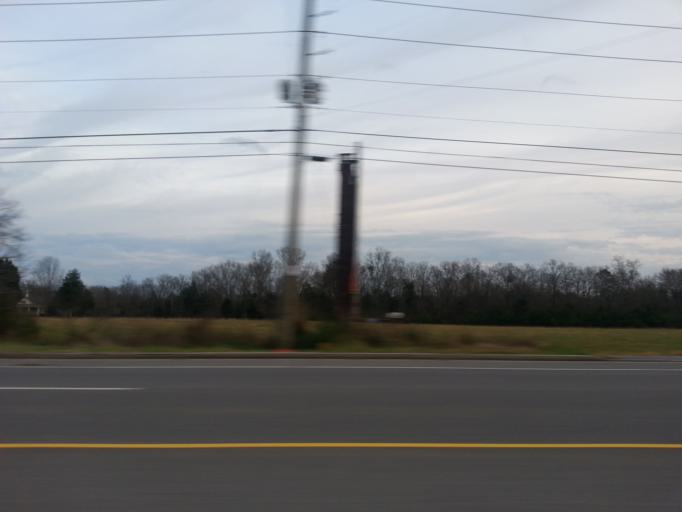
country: US
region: Tennessee
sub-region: Monroe County
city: Madisonville
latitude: 35.5023
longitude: -84.3822
